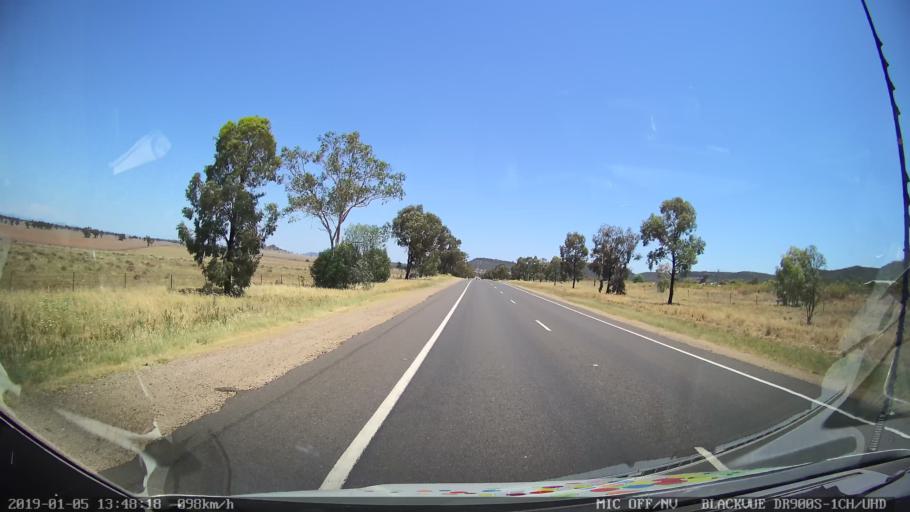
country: AU
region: New South Wales
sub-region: Gunnedah
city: Gunnedah
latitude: -30.9999
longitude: 150.2787
